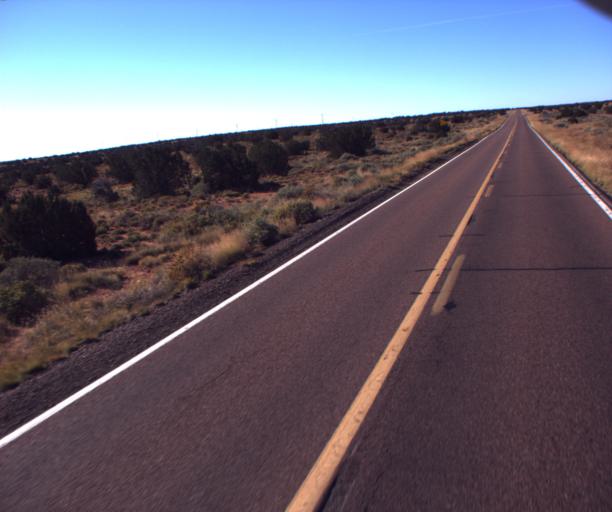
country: US
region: Arizona
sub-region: Navajo County
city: Holbrook
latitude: 34.7028
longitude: -110.3025
